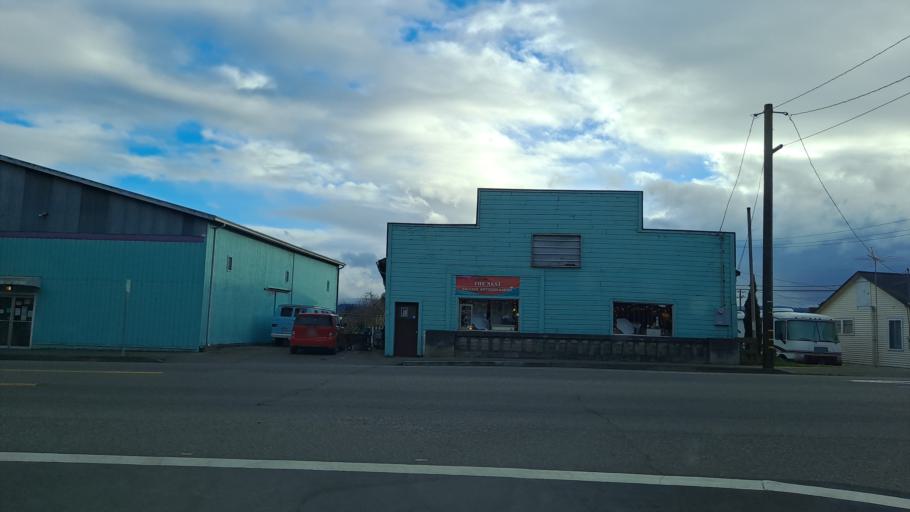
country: US
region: California
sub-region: Humboldt County
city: Fortuna
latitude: 40.5980
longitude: -124.1498
